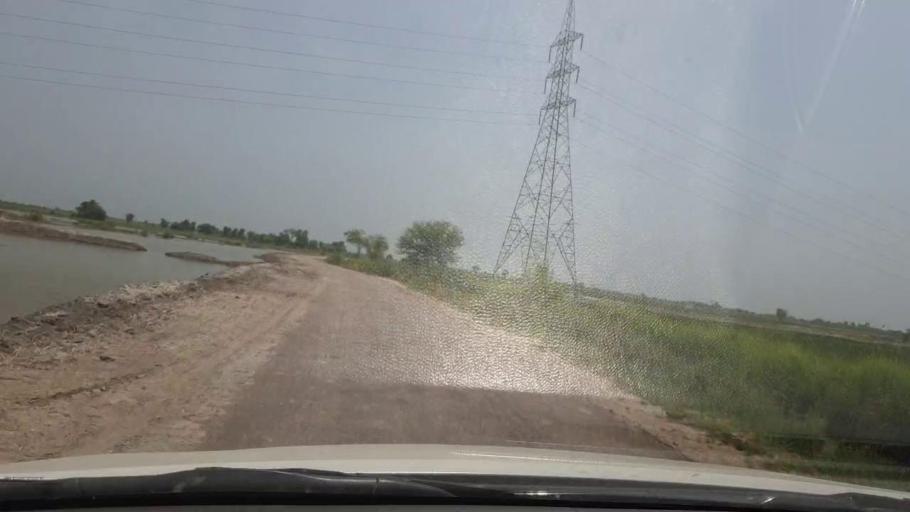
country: PK
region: Sindh
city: Shikarpur
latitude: 28.0914
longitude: 68.6195
